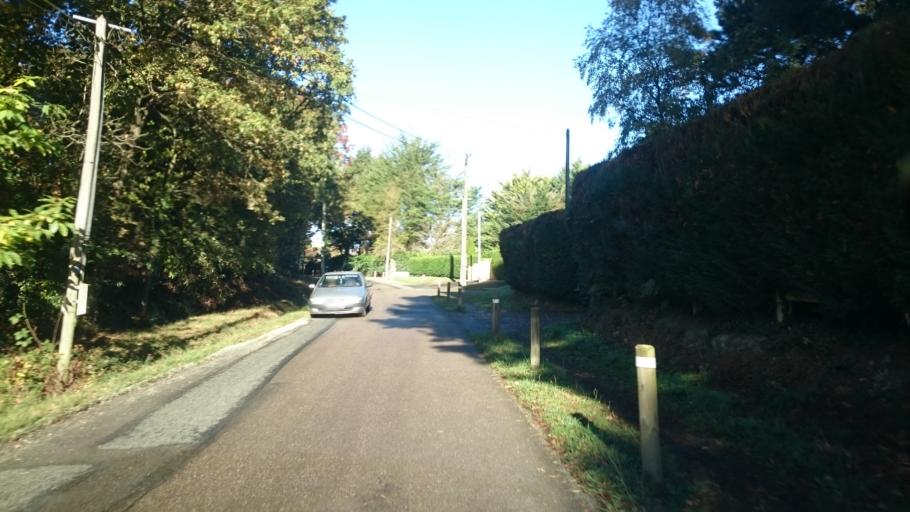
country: FR
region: Brittany
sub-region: Departement d'Ille-et-Vilaine
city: Laille
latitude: 47.9692
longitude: -1.7086
